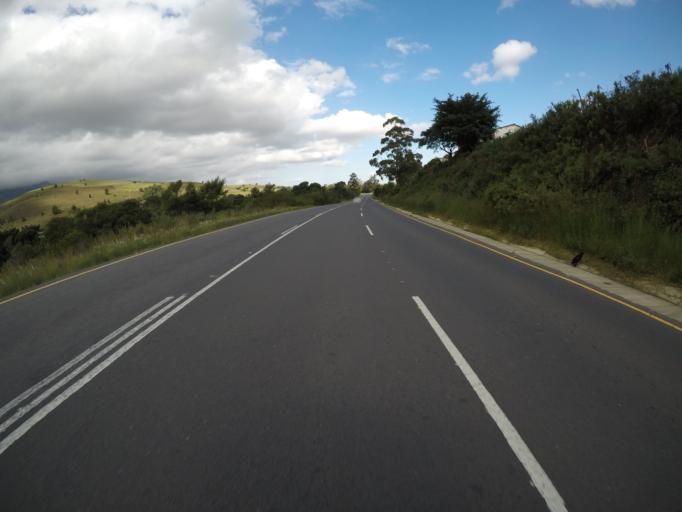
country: ZA
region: Western Cape
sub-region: Overberg District Municipality
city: Swellendam
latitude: -34.0006
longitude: 20.3698
